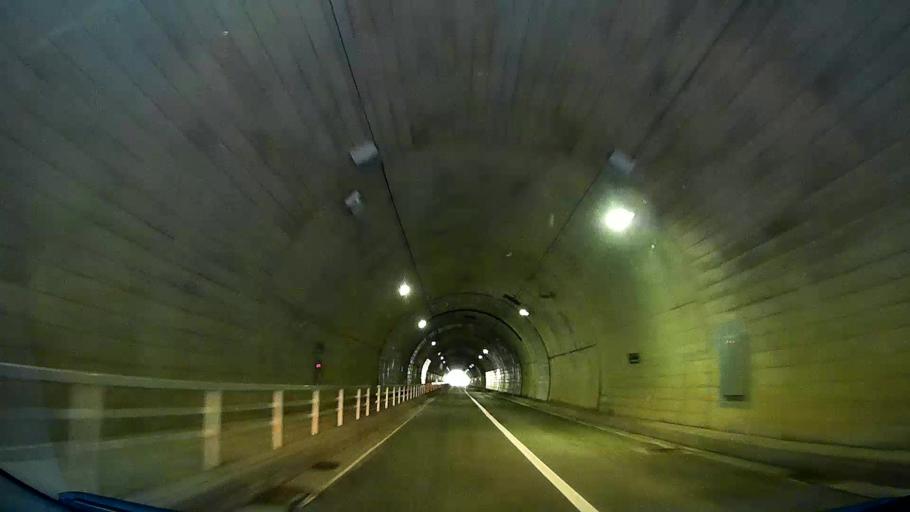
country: JP
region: Hokkaido
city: Sapporo
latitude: 42.9962
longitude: 141.1571
